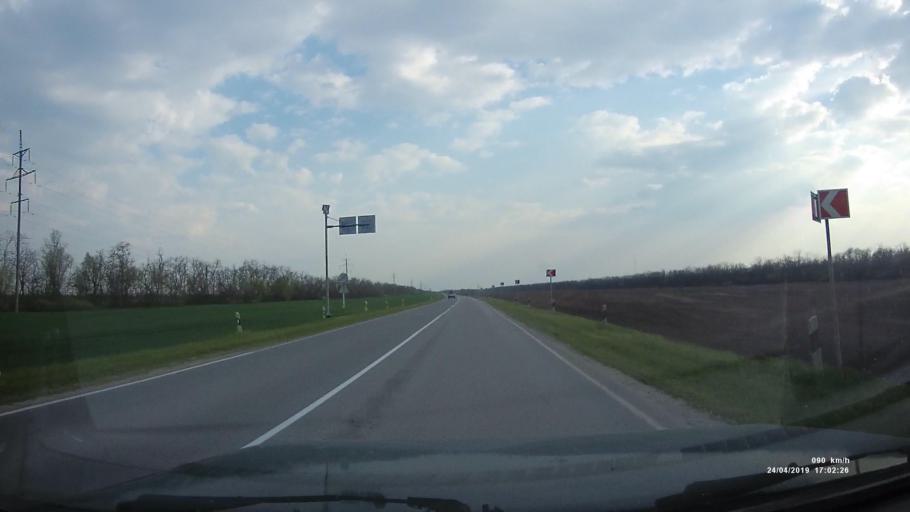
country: RU
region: Rostov
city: Sal'sk
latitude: 46.5806
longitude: 41.6155
